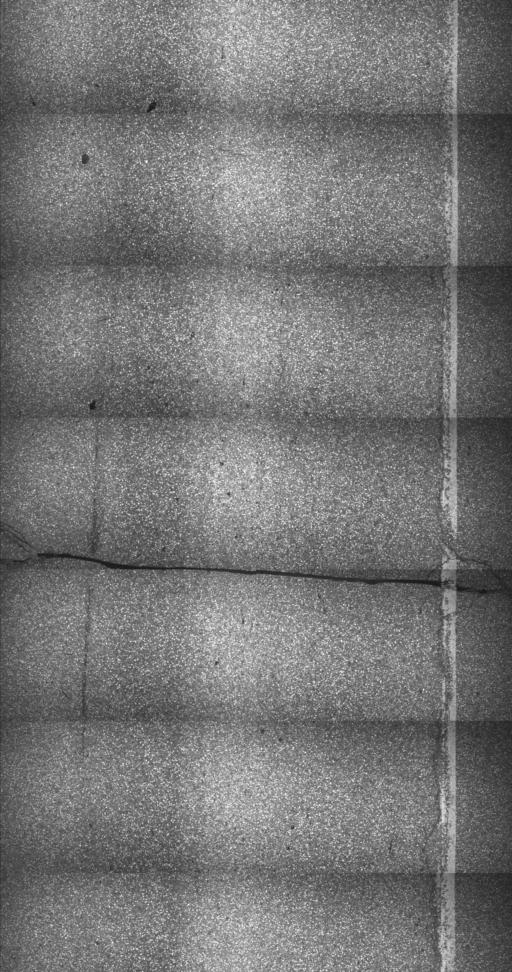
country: US
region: Vermont
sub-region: Franklin County
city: Richford
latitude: 44.9476
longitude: -72.7054
